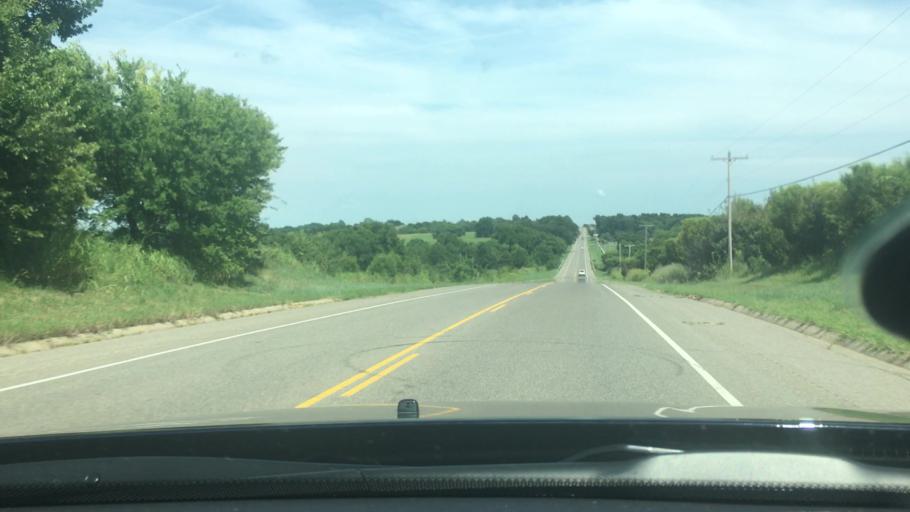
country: US
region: Oklahoma
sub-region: Pottawatomie County
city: Shawnee
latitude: 35.3331
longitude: -96.8360
